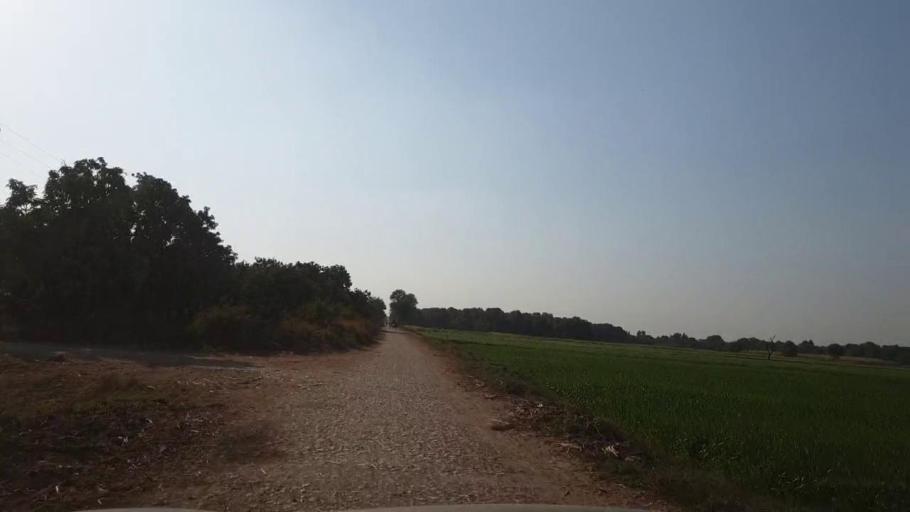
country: PK
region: Sindh
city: Tando Allahyar
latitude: 25.5704
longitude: 68.6509
